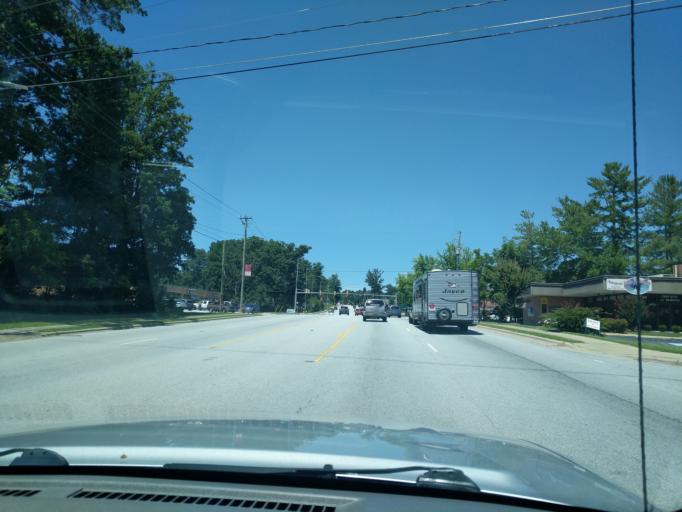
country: US
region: North Carolina
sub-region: Henderson County
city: Fletcher
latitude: 35.4339
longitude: -82.5016
